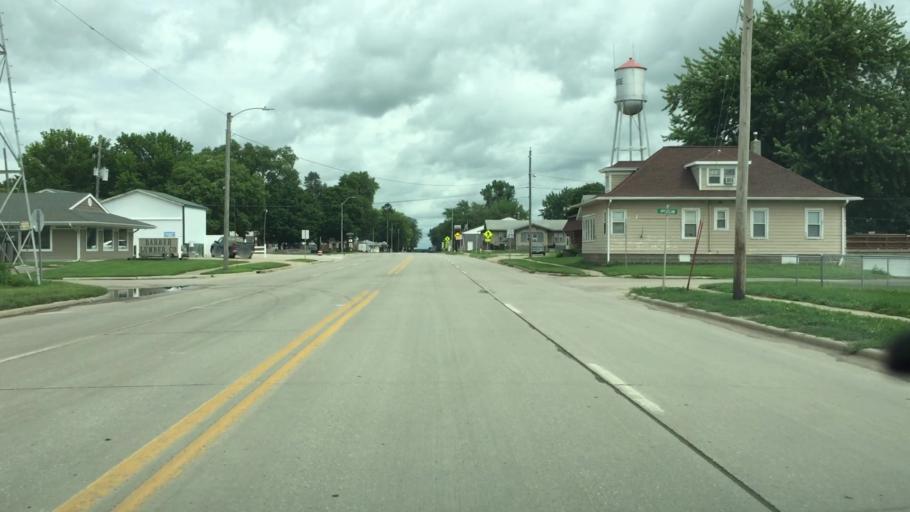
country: US
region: Iowa
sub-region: Jasper County
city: Monroe
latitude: 41.5203
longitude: -93.1018
